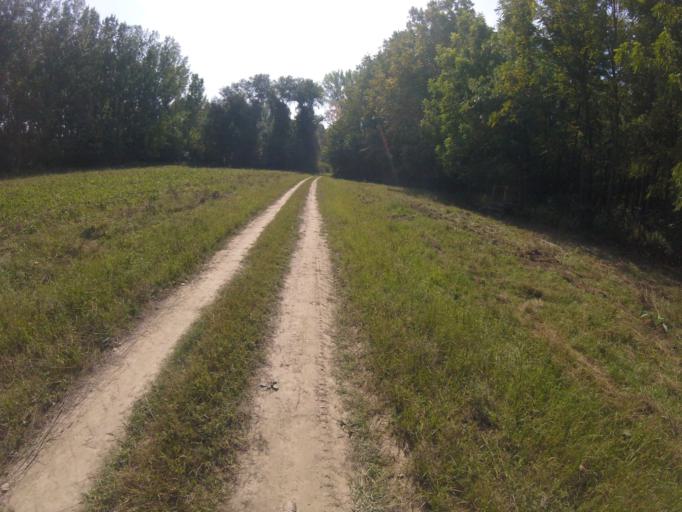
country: HU
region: Bacs-Kiskun
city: Baja
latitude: 46.2233
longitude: 18.8837
